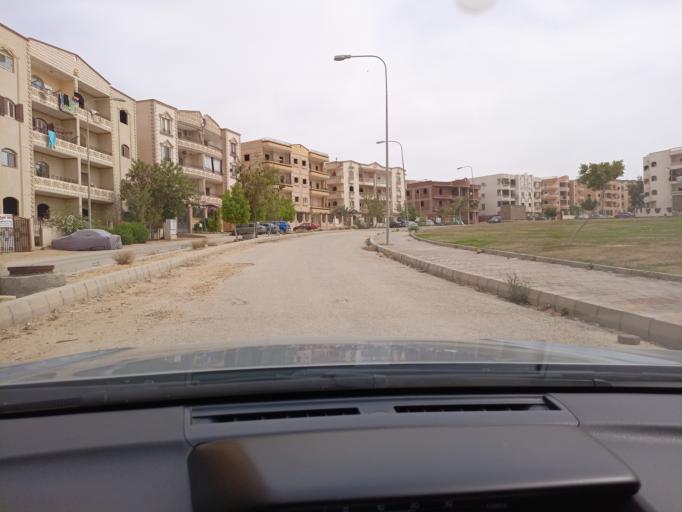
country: EG
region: Muhafazat al Qalyubiyah
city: Al Khankah
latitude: 30.2440
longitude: 31.4884
